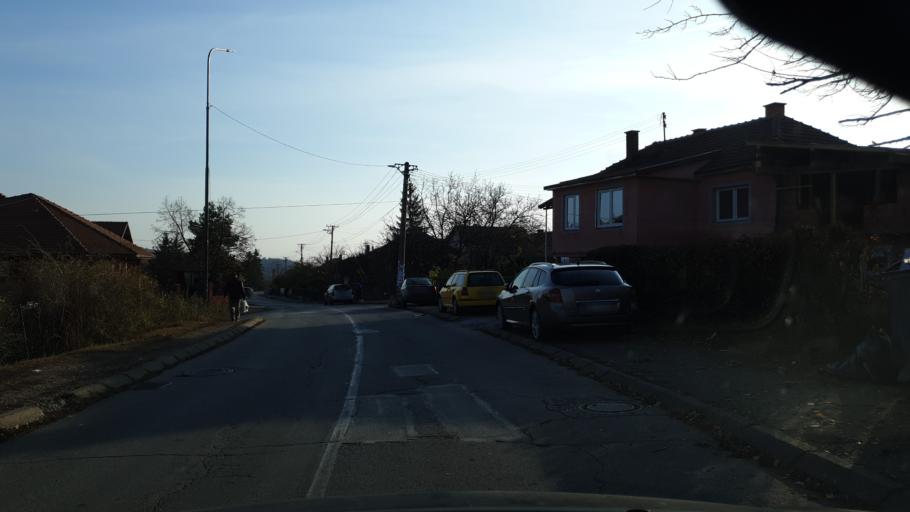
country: RS
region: Central Serbia
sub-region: Borski Okrug
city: Bor
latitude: 44.0542
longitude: 22.1008
